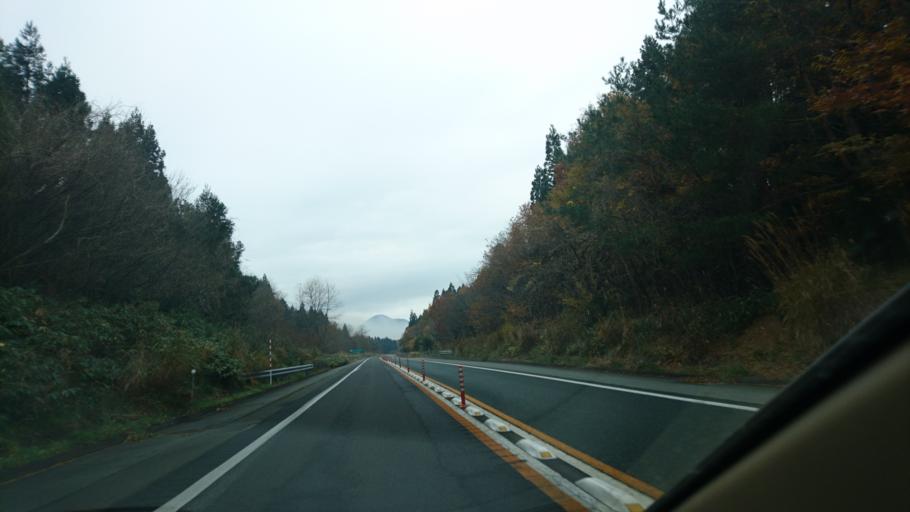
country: JP
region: Iwate
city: Kitakami
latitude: 39.2816
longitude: 141.0081
